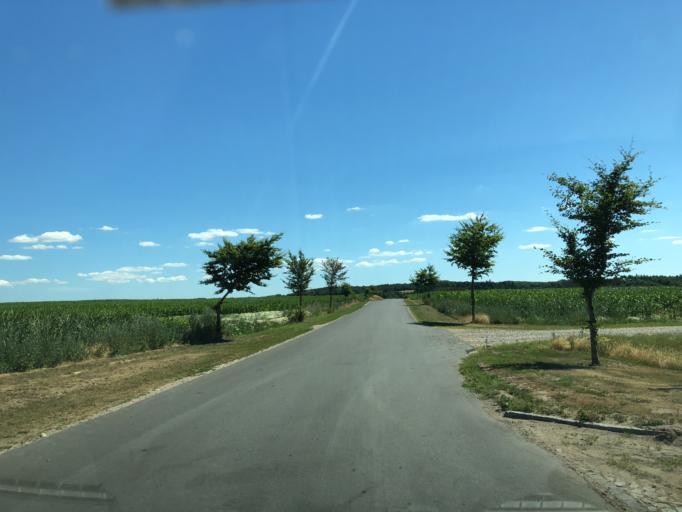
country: DK
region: Central Jutland
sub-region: Viborg Kommune
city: Bjerringbro
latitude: 56.5114
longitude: 9.5679
